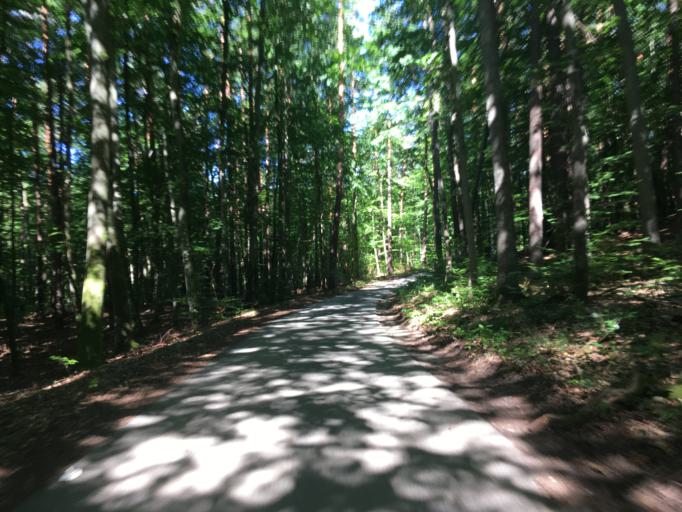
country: DE
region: Brandenburg
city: Furstenberg
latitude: 53.1635
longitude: 13.0546
